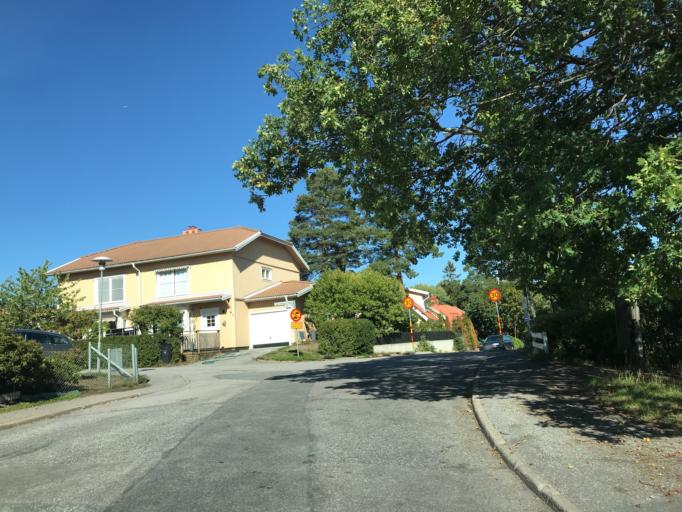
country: SE
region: Stockholm
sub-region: Sollentuna Kommun
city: Sollentuna
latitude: 59.4210
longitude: 17.9495
